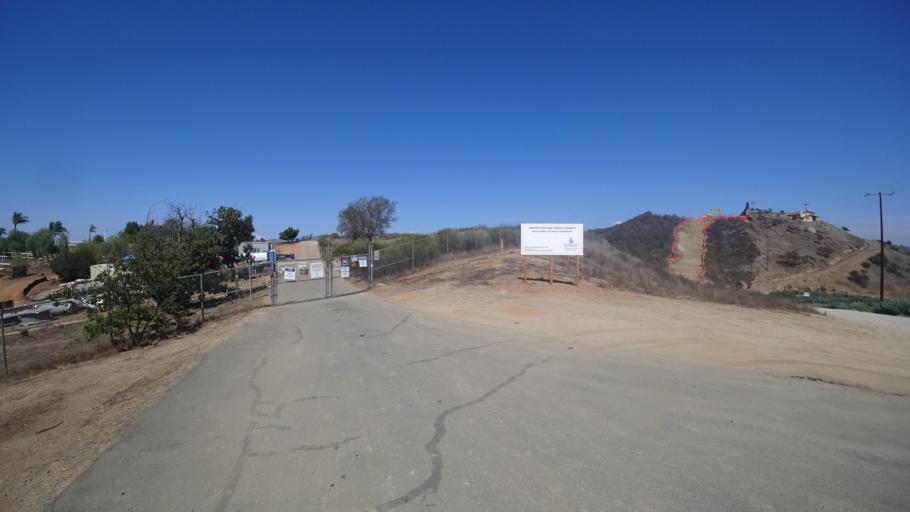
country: US
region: California
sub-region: San Diego County
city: Hidden Meadows
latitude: 33.2786
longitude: -117.1095
